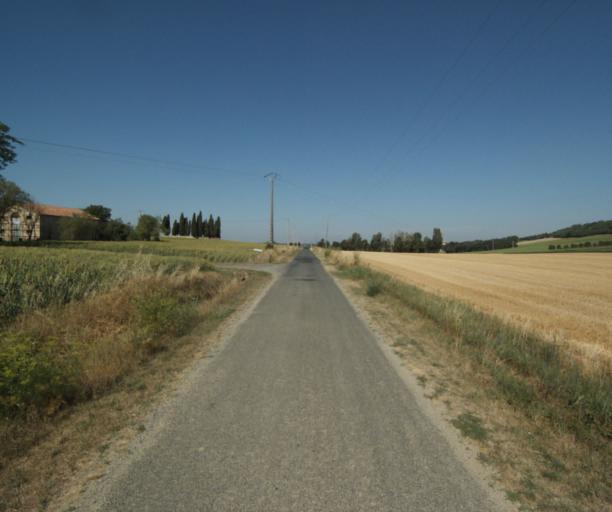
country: FR
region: Midi-Pyrenees
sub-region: Departement de la Haute-Garonne
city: Saint-Felix-Lauragais
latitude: 43.5087
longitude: 1.9295
